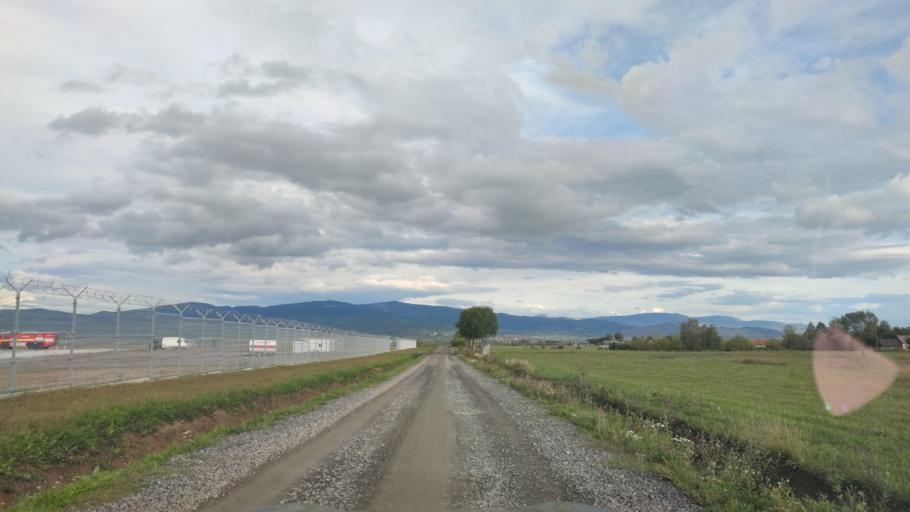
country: RO
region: Harghita
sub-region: Comuna Subcetate
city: Subcetate
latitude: 46.8176
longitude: 25.4106
